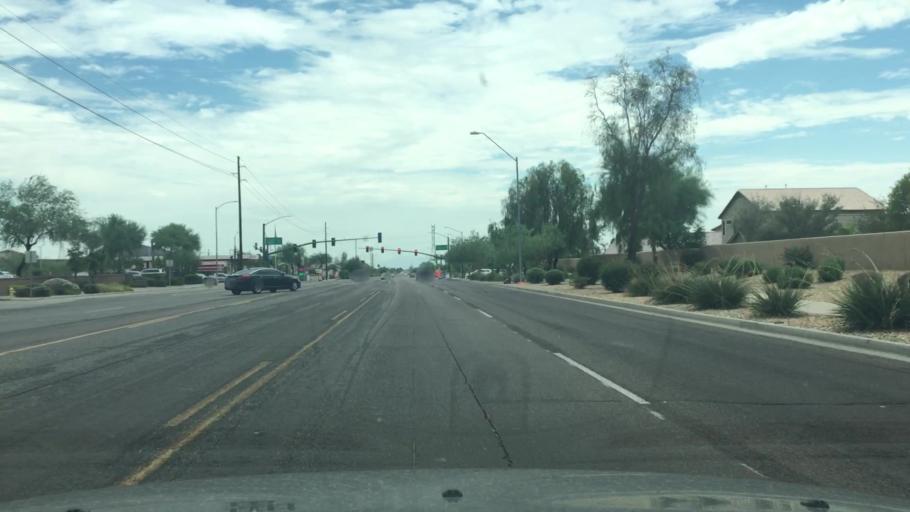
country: US
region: Arizona
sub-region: Maricopa County
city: Sun City
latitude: 33.7137
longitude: -112.2032
